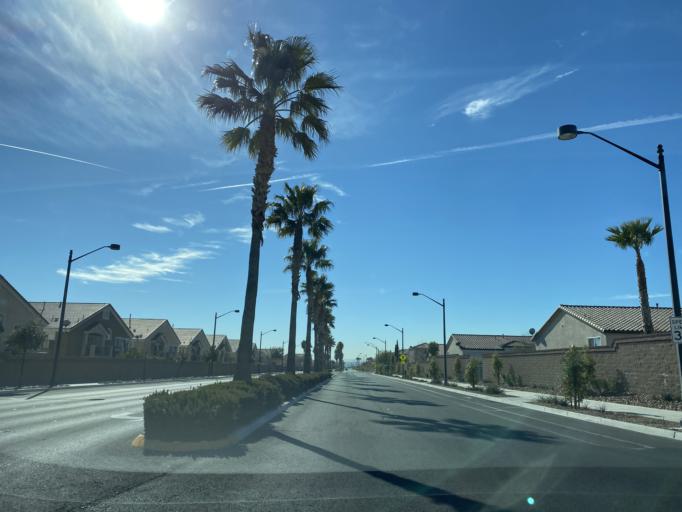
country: US
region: Nevada
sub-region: Clark County
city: Summerlin South
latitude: 36.2900
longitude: -115.2970
